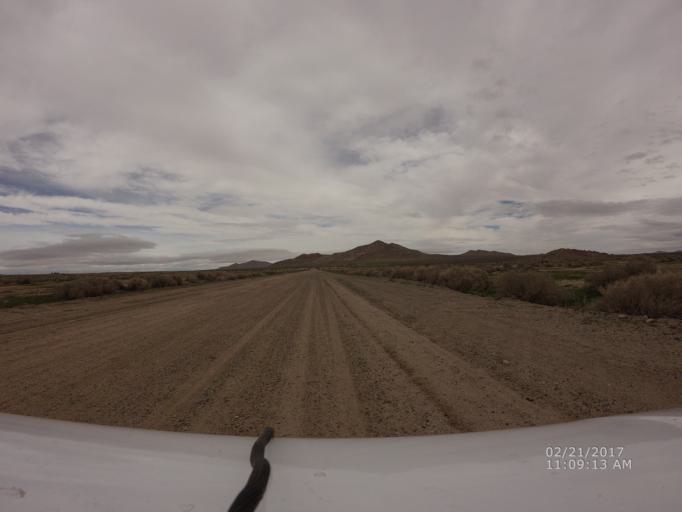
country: US
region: California
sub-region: Los Angeles County
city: Lake Los Angeles
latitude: 34.6420
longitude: -117.8094
